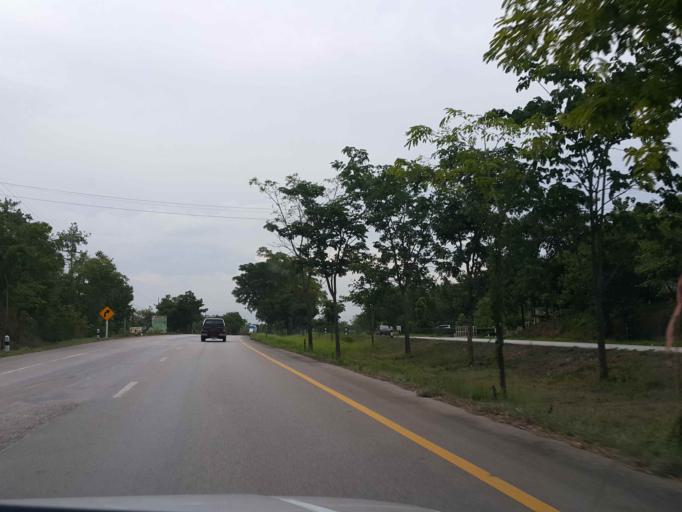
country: TH
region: Lampang
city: Ko Kha
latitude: 18.1284
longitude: 99.3910
